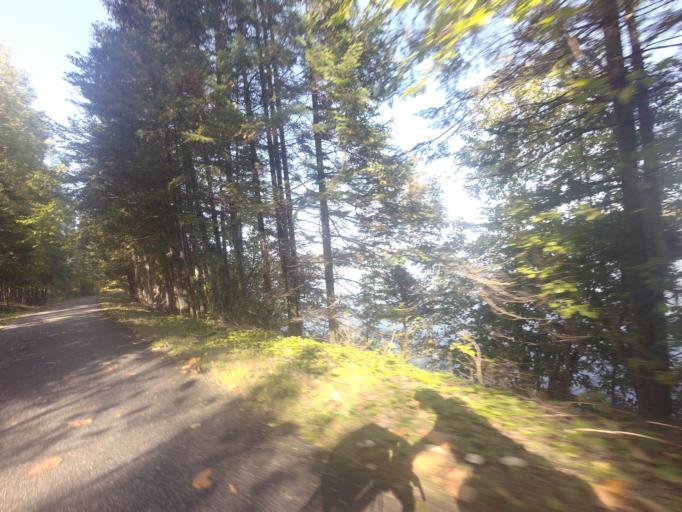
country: CA
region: Quebec
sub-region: Laurentides
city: Mont-Laurier
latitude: 46.5074
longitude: -75.3972
